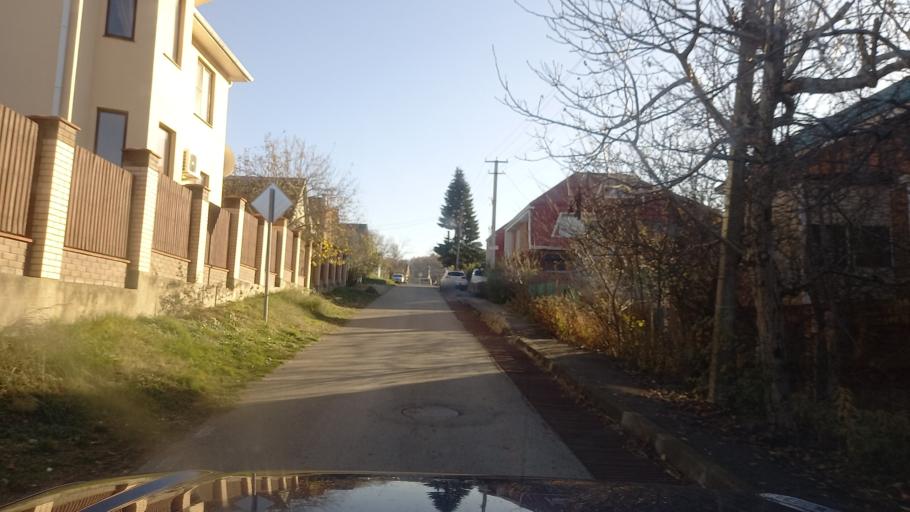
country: RU
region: Krasnodarskiy
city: Goryachiy Klyuch
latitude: 44.6208
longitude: 39.1040
